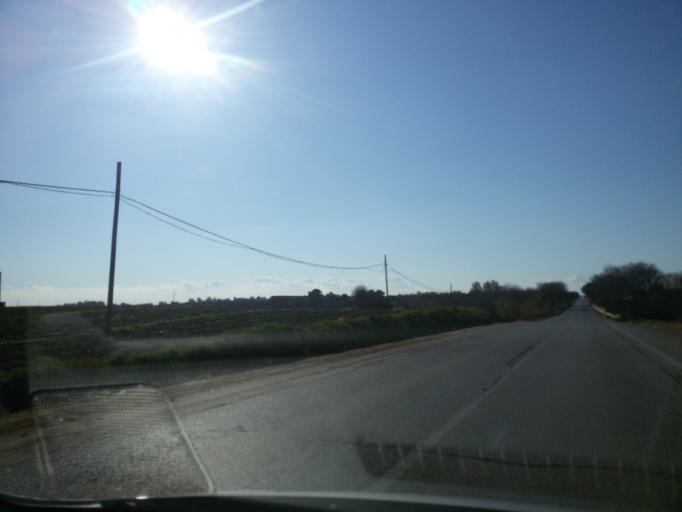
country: IT
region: Apulia
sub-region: Provincia di Brindisi
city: Brindisi
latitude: 40.6485
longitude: 17.8603
